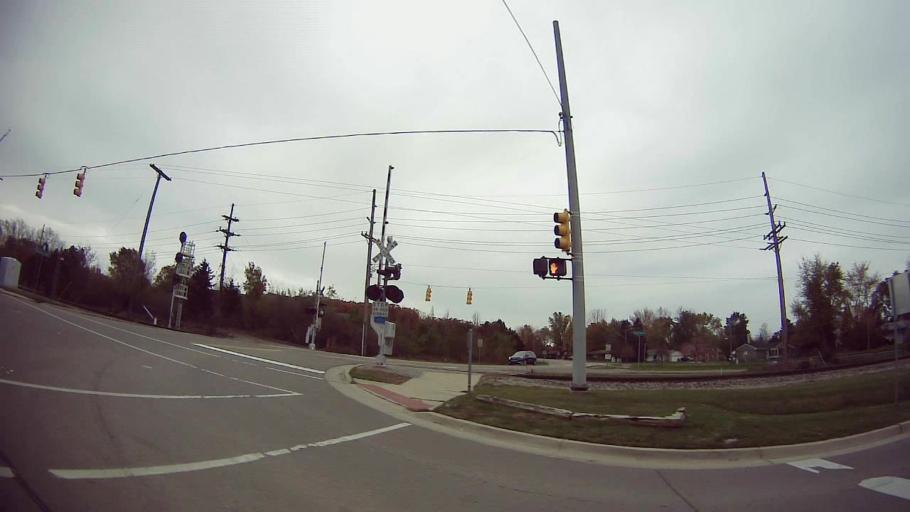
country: US
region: Michigan
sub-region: Oakland County
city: Waterford
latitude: 42.6760
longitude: -83.3566
